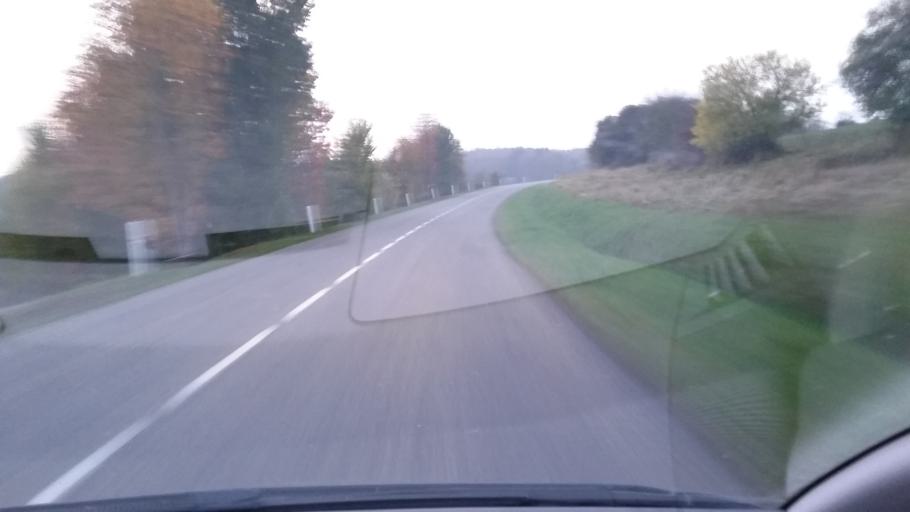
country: FR
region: Lorraine
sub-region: Departement de la Moselle
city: Soucht
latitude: 48.8643
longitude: 7.3094
